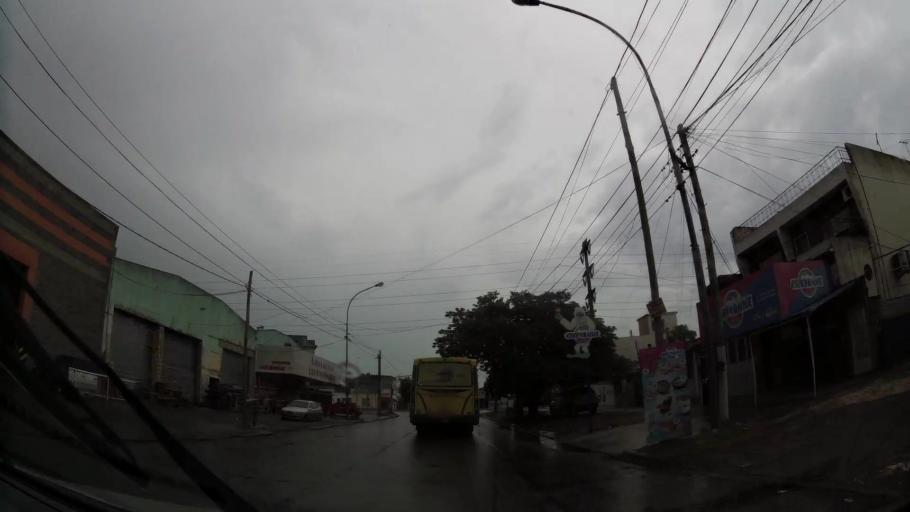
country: AR
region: Buenos Aires
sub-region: Partido de Quilmes
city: Quilmes
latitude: -34.7724
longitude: -58.2294
